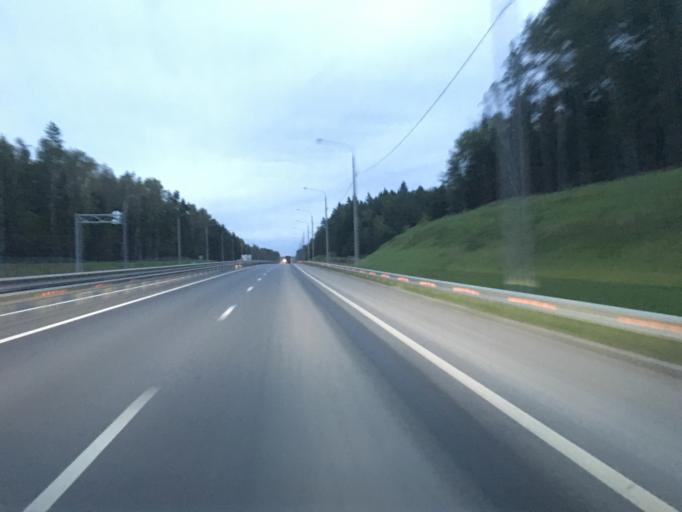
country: RU
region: Kaluga
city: Maloyaroslavets
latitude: 54.9289
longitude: 36.4117
